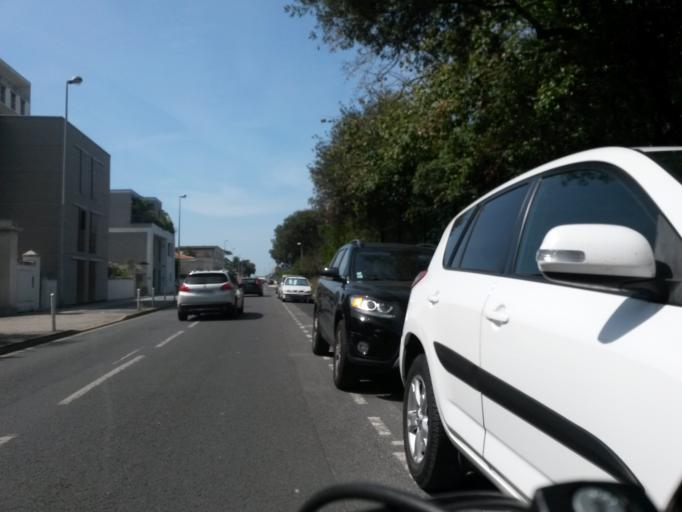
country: FR
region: Poitou-Charentes
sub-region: Departement de la Charente-Maritime
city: La Rochelle
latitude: 46.1543
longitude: -1.1724
